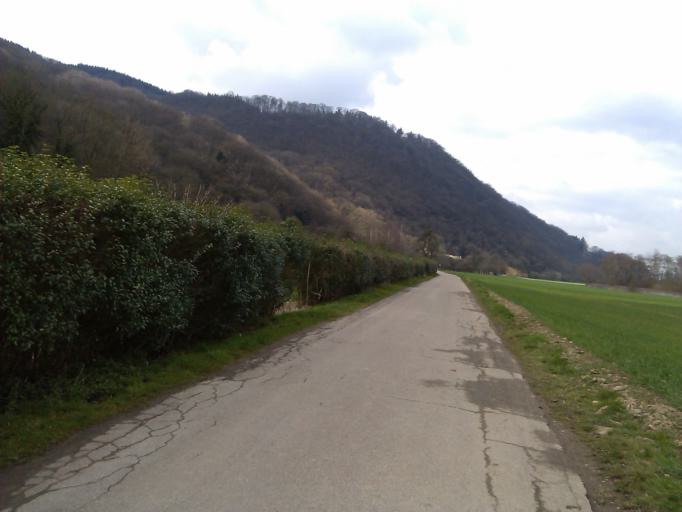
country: DE
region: Rheinland-Pfalz
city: Hammerstein
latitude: 50.4600
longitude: 7.3534
